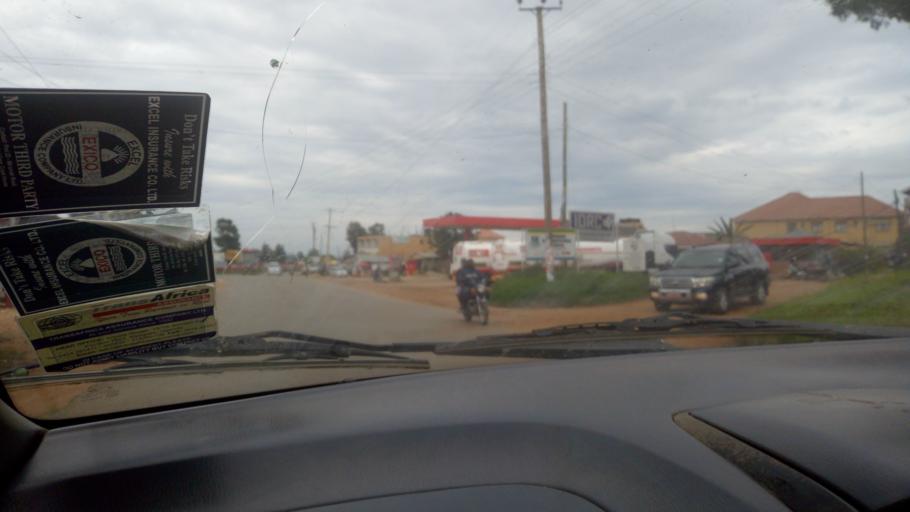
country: UG
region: Western Region
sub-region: Mbarara District
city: Mbarara
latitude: -0.6040
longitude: 30.6480
